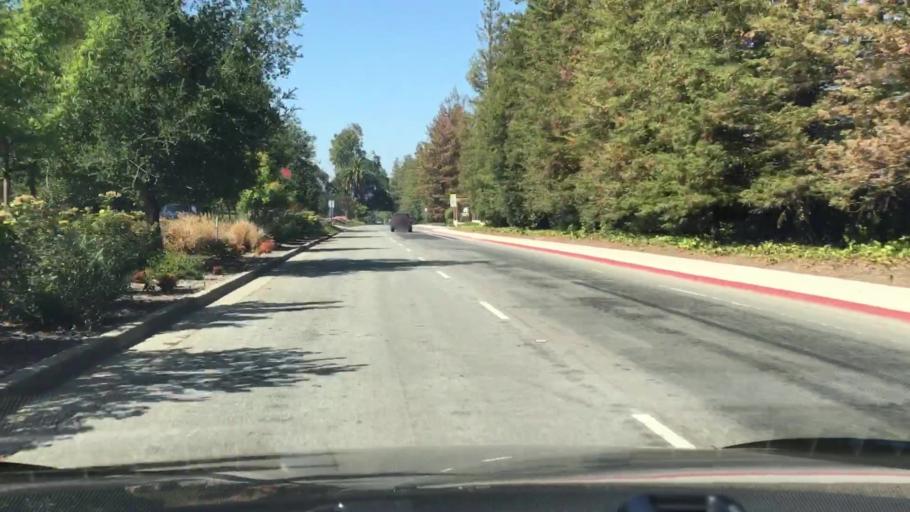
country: US
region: California
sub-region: Santa Clara County
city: Saratoga
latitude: 37.2627
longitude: -122.0138
